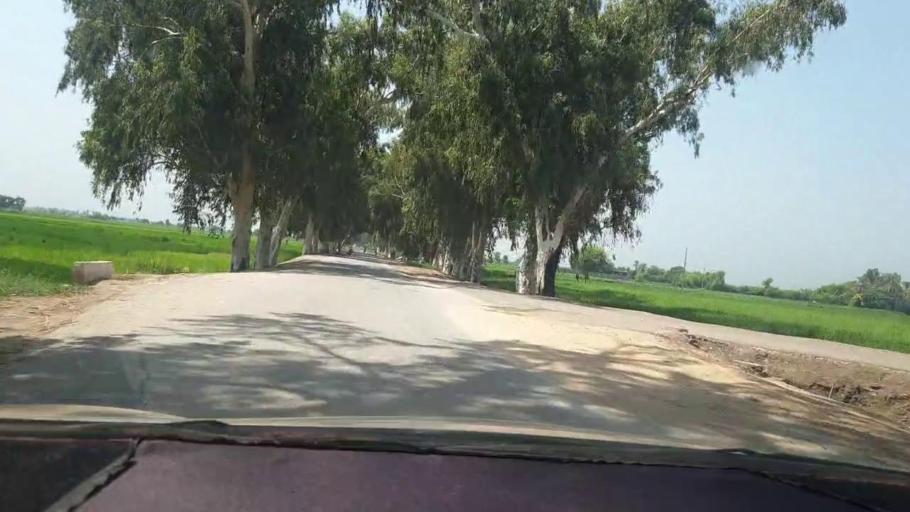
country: PK
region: Sindh
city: Kambar
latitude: 27.6080
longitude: 68.0421
